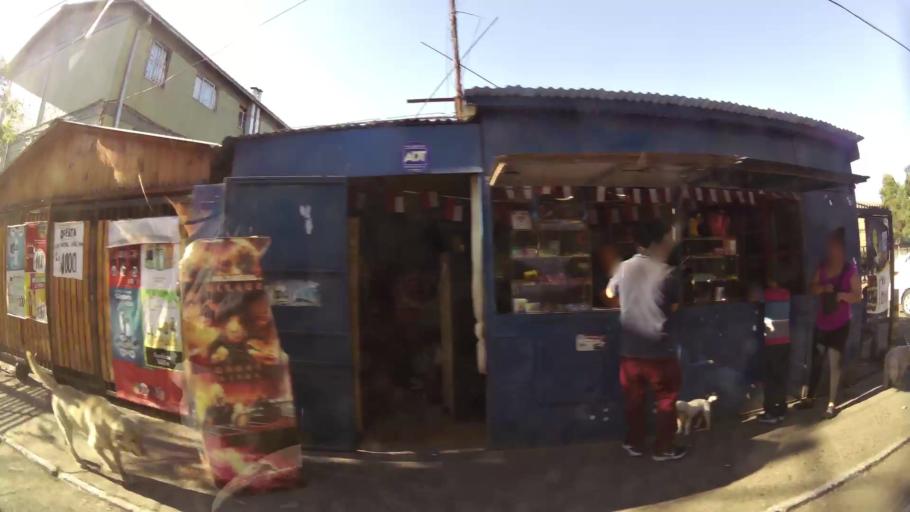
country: CL
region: Santiago Metropolitan
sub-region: Provincia de Talagante
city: Penaflor
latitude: -33.6029
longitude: -70.8622
